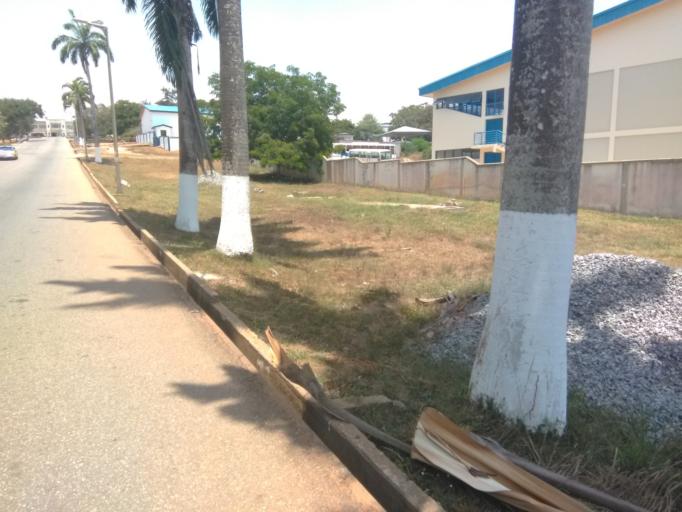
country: GH
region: Central
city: Cape Coast
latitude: 5.1030
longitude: -1.2842
